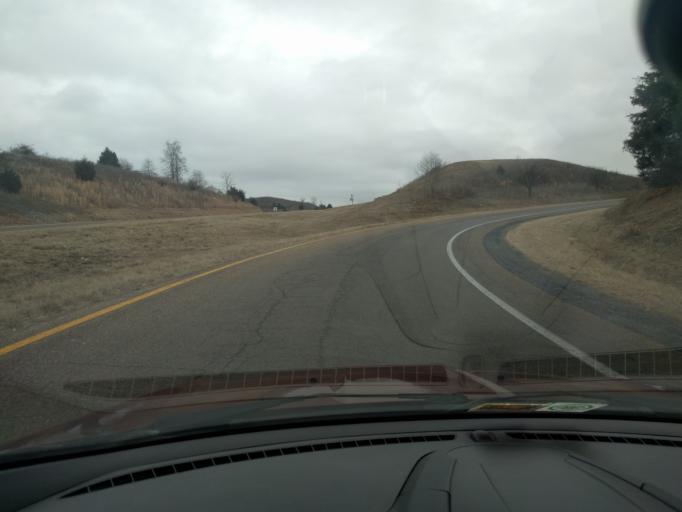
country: US
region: Virginia
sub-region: Augusta County
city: Jolivue
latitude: 38.1205
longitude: -79.0685
